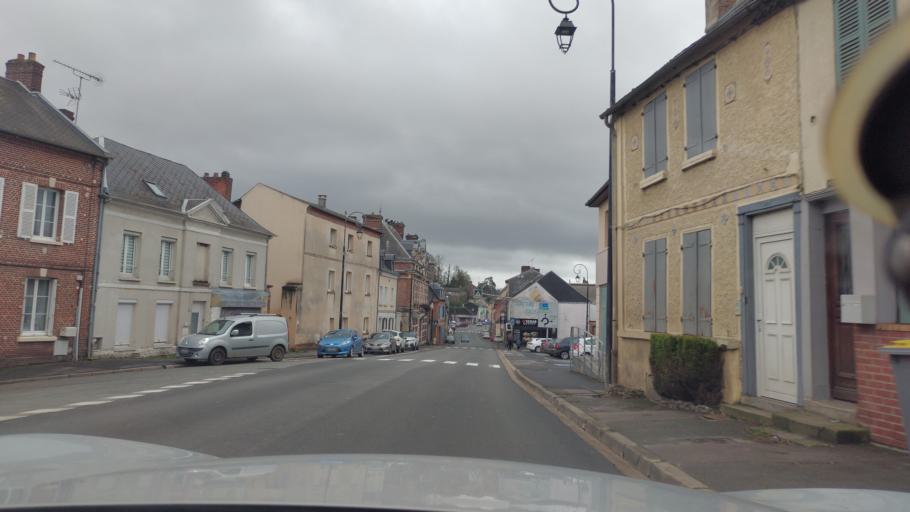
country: FR
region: Picardie
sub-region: Departement de l'Oise
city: Saint-Omer-en-Chaussee
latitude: 49.5761
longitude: 1.9547
